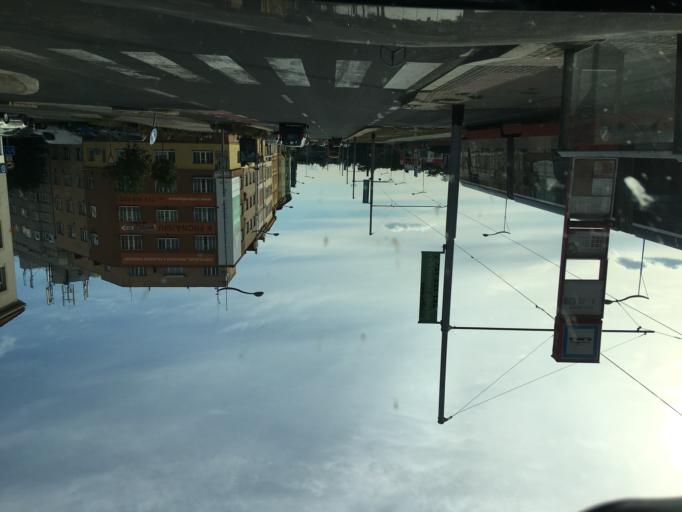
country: CZ
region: Praha
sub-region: Praha 8
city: Liben
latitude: 50.1036
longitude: 14.4881
